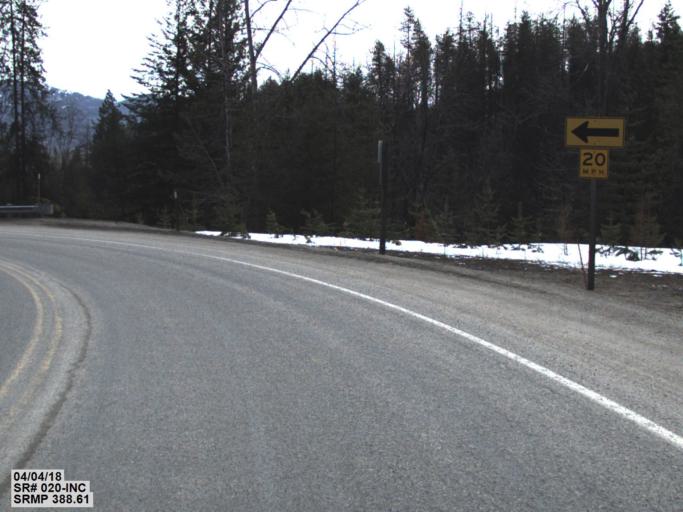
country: CA
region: British Columbia
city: Fruitvale
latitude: 48.6805
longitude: -117.4310
